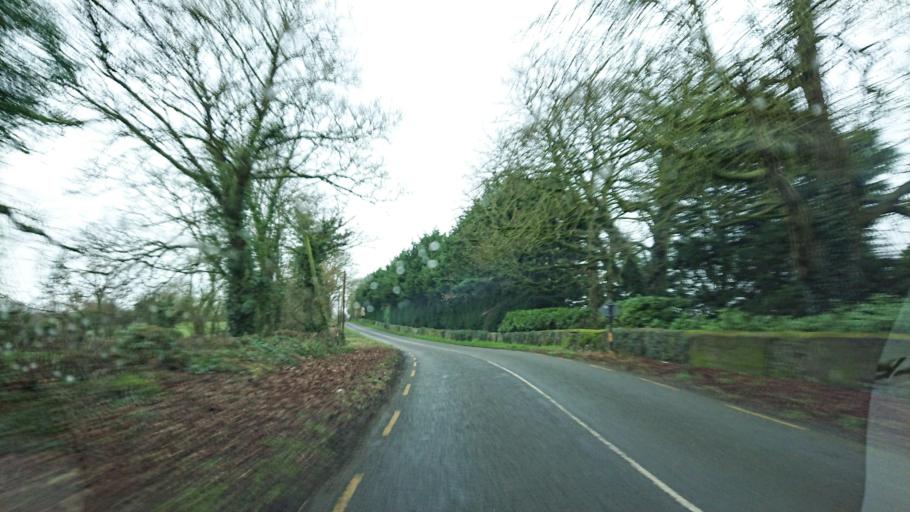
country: IE
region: Leinster
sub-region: Kilkenny
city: Callan
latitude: 52.5361
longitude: -7.2924
